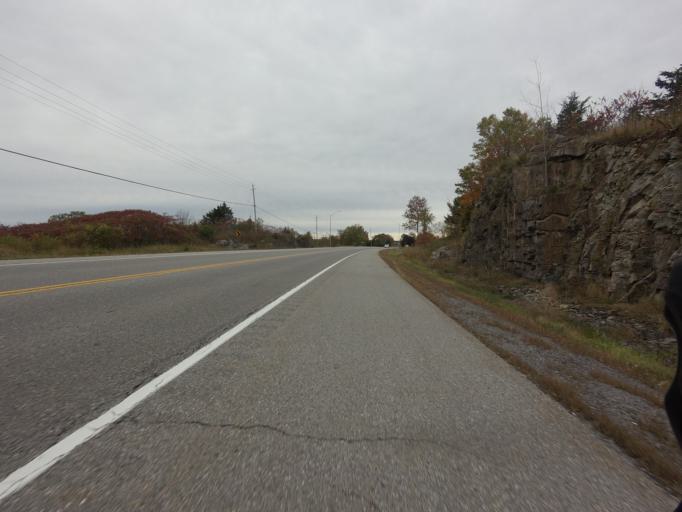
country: CA
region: Ontario
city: Gananoque
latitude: 44.4536
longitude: -76.2673
